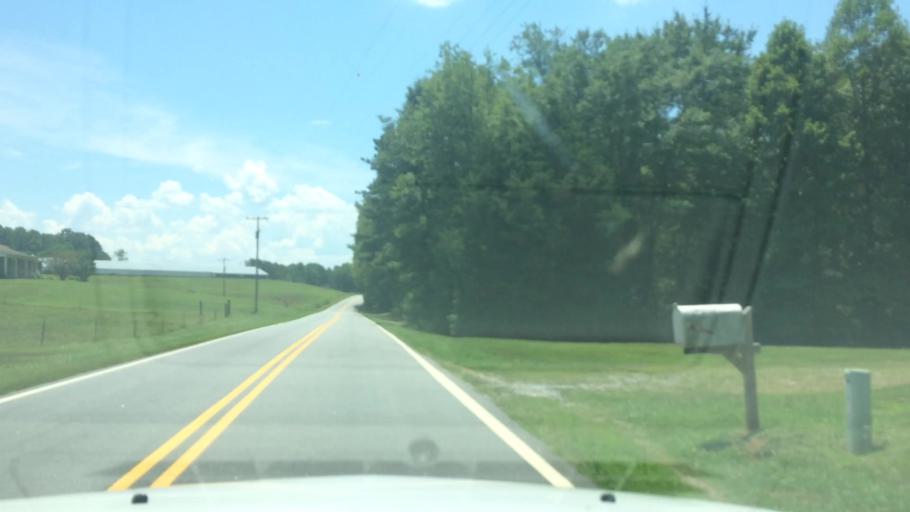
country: US
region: North Carolina
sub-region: Alexander County
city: Taylorsville
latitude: 35.9295
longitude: -81.2628
